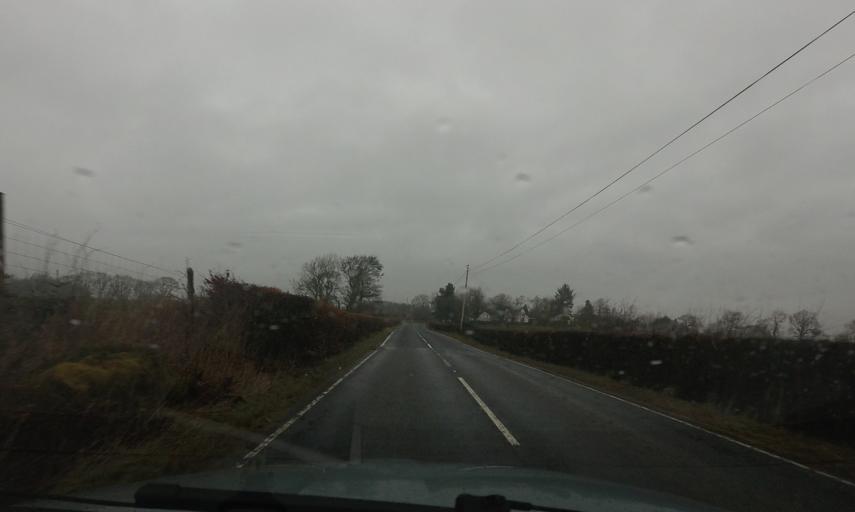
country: GB
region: Scotland
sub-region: Stirling
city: Balfron
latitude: 56.1092
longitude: -4.3582
